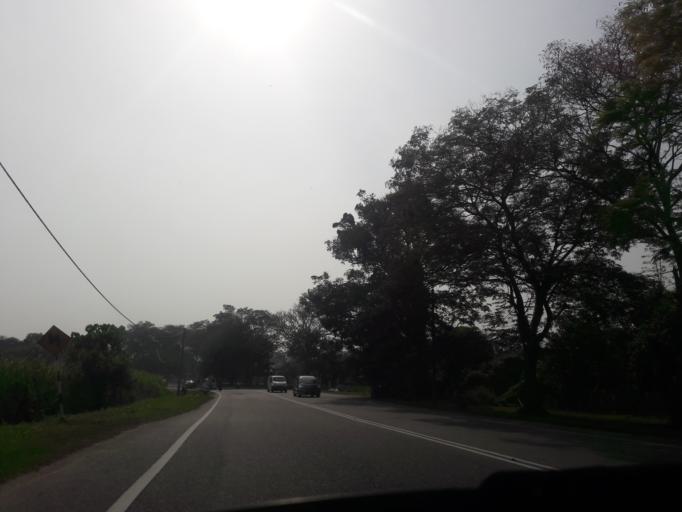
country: MY
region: Kedah
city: Kulim
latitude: 5.3466
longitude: 100.5214
